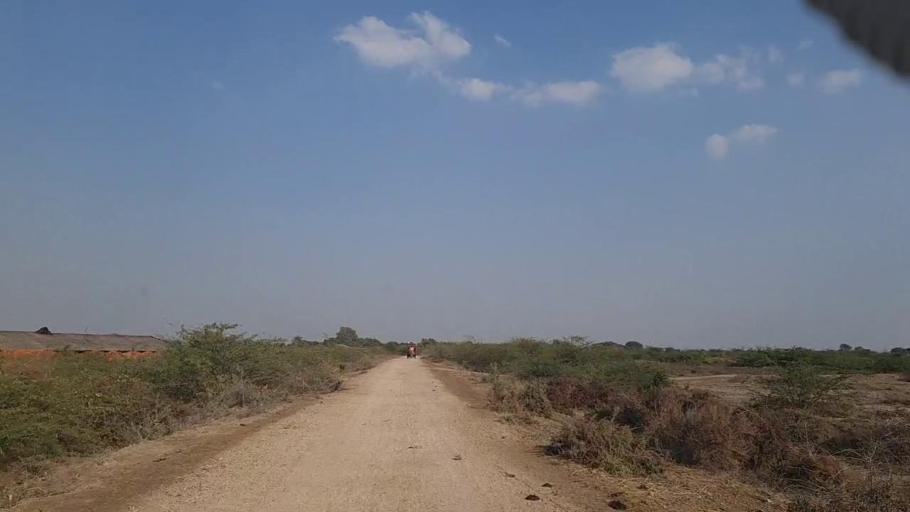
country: PK
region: Sindh
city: Jati
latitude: 24.4296
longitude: 68.3744
